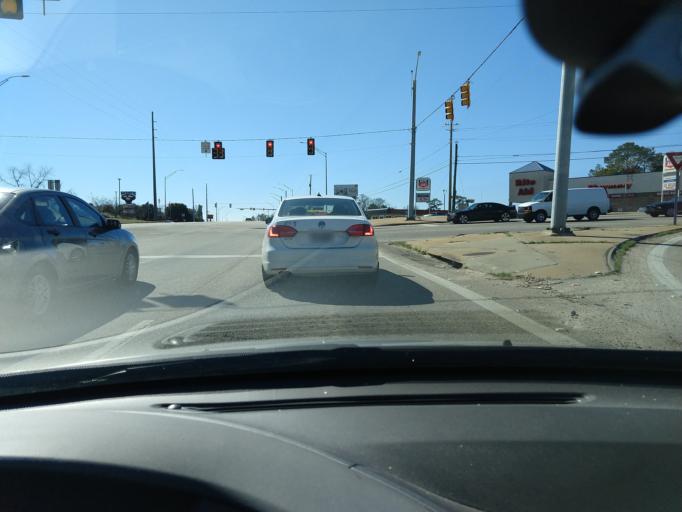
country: US
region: Alabama
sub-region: Covington County
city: Andalusia
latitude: 31.3178
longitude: -86.4974
